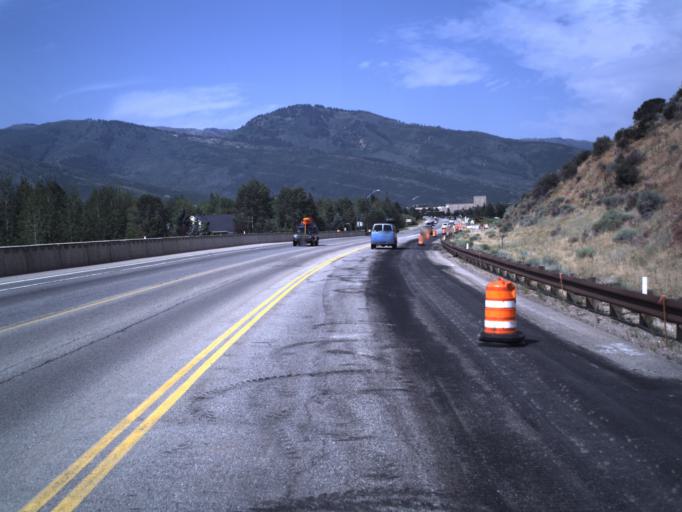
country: US
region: Utah
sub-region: Summit County
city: Park City
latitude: 40.6686
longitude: -111.4834
